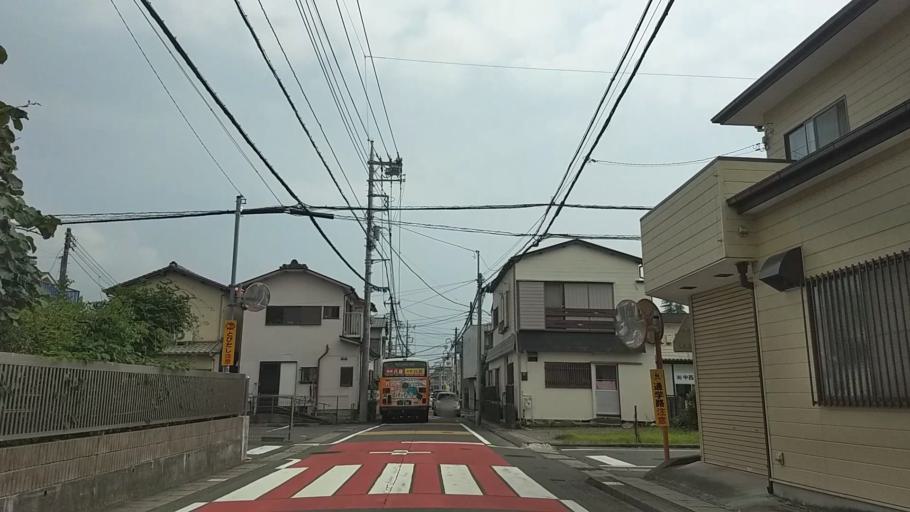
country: JP
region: Shizuoka
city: Mishima
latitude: 35.1155
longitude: 138.9322
